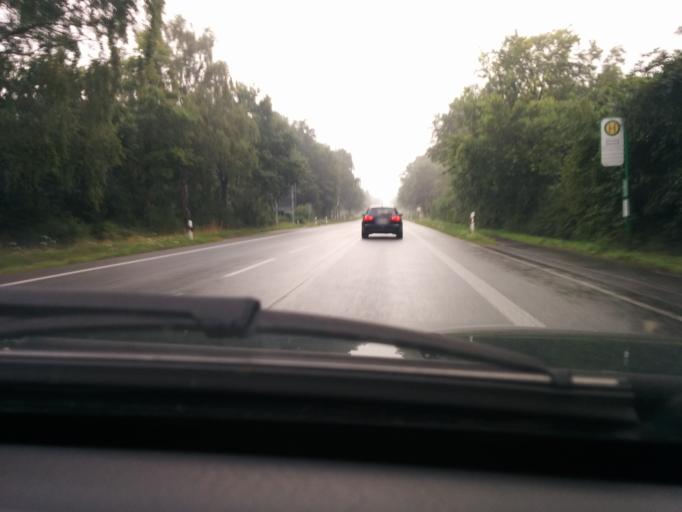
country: DE
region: North Rhine-Westphalia
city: Halle
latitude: 52.0438
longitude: 8.3865
